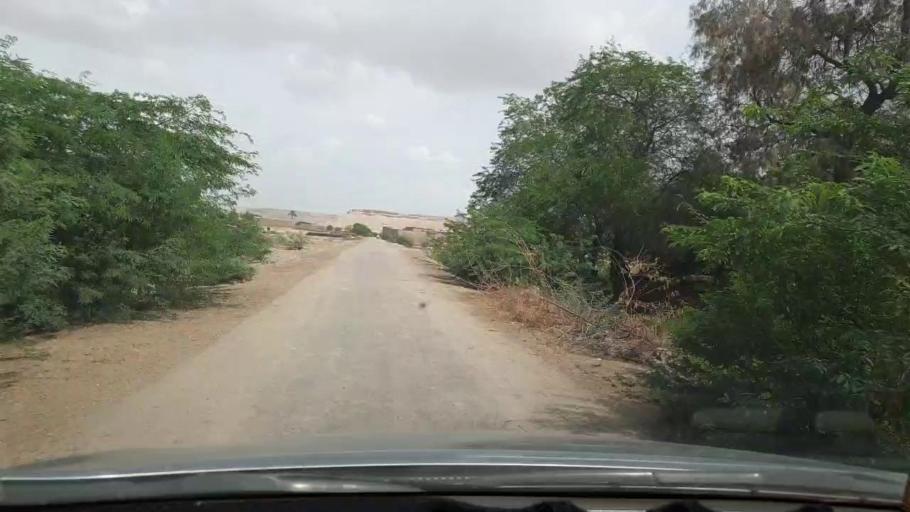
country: PK
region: Sindh
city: Khairpur
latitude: 27.4786
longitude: 68.8552
